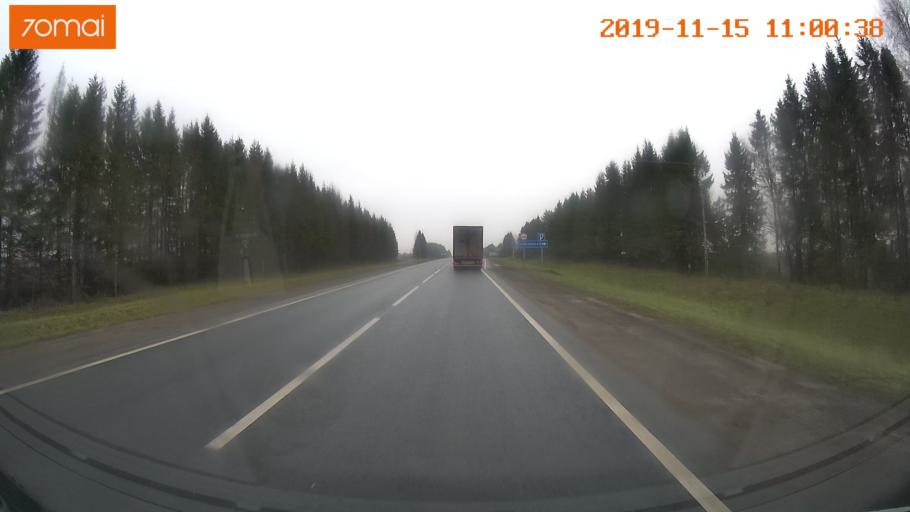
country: RU
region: Vologda
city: Chebsara
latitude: 59.1364
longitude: 38.9040
